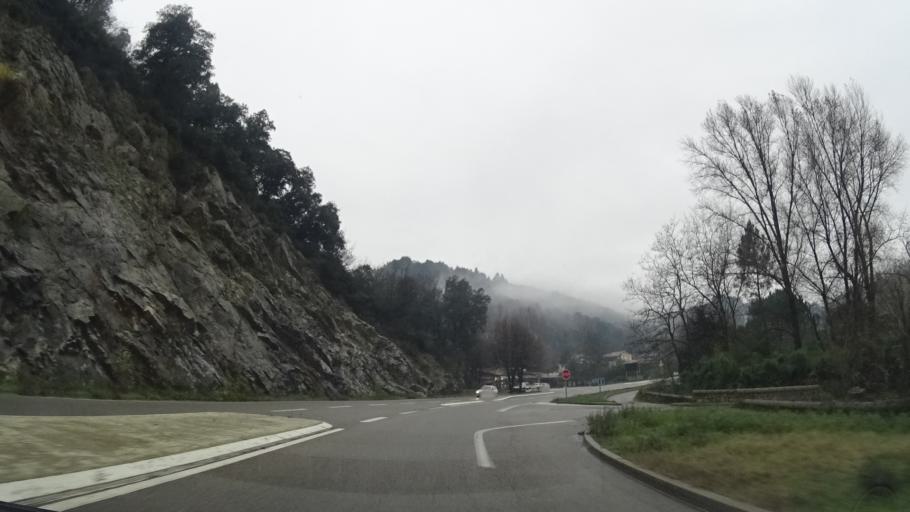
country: FR
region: Rhone-Alpes
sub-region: Departement de l'Ardeche
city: Jaujac
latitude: 44.6569
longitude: 4.2983
